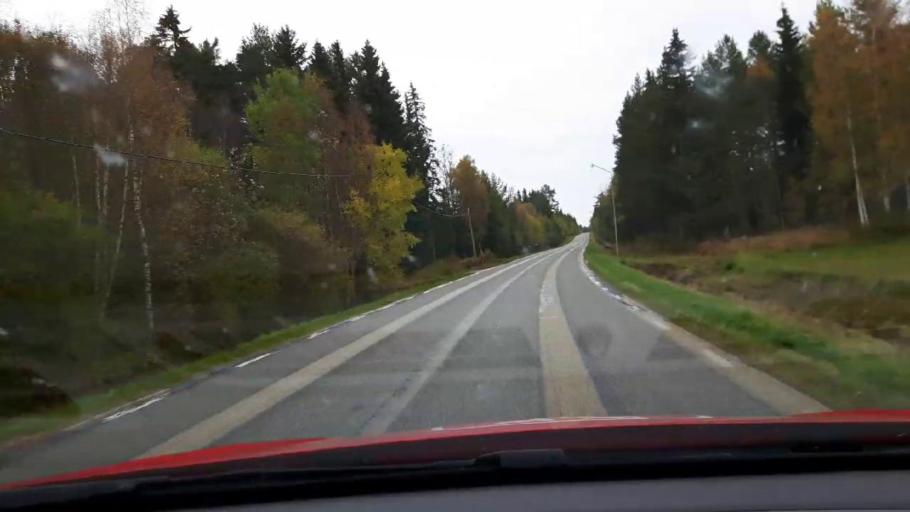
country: SE
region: Jaemtland
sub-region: Bergs Kommun
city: Hoverberg
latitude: 62.8939
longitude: 14.3493
